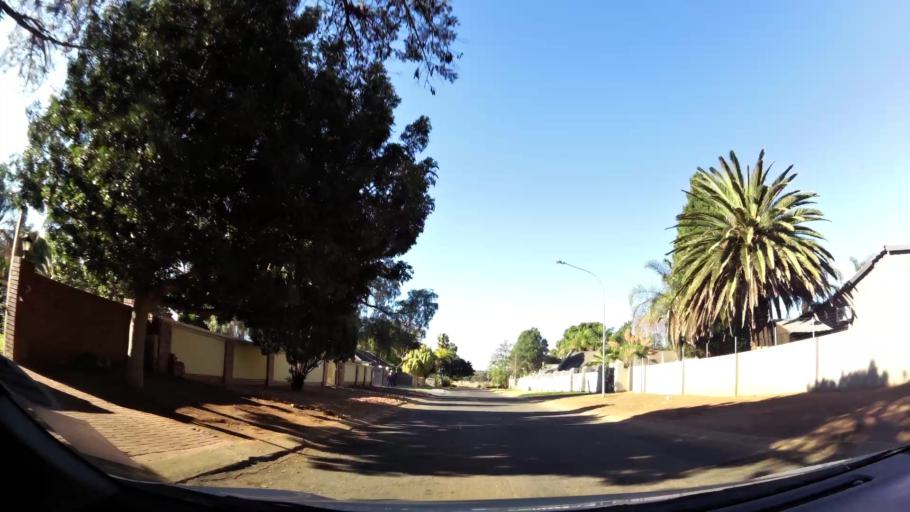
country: ZA
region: Limpopo
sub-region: Capricorn District Municipality
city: Polokwane
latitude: -23.8810
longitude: 29.4912
